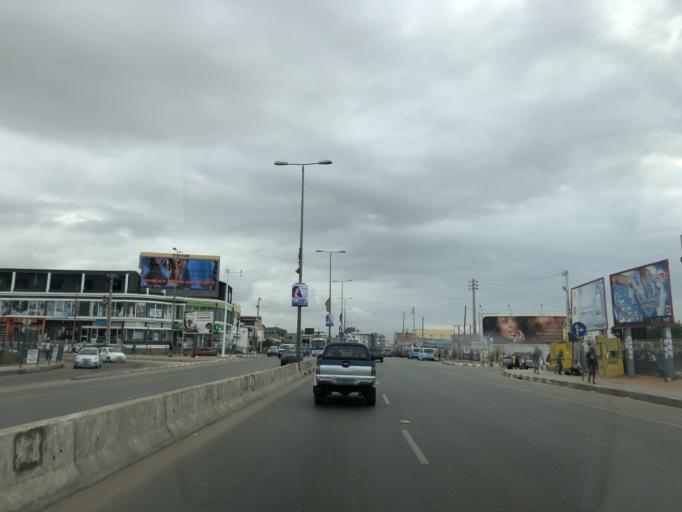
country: AO
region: Luanda
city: Luanda
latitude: -8.8858
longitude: 13.2063
